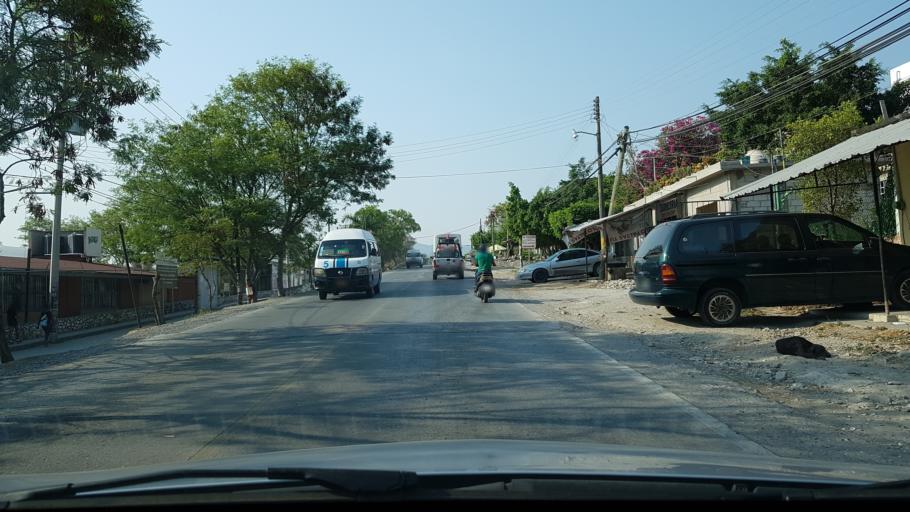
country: MX
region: Morelos
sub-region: Tlaquiltenango
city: Alfredo V. Bonfil (Chacampalco)
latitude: 18.6569
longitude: -99.1546
